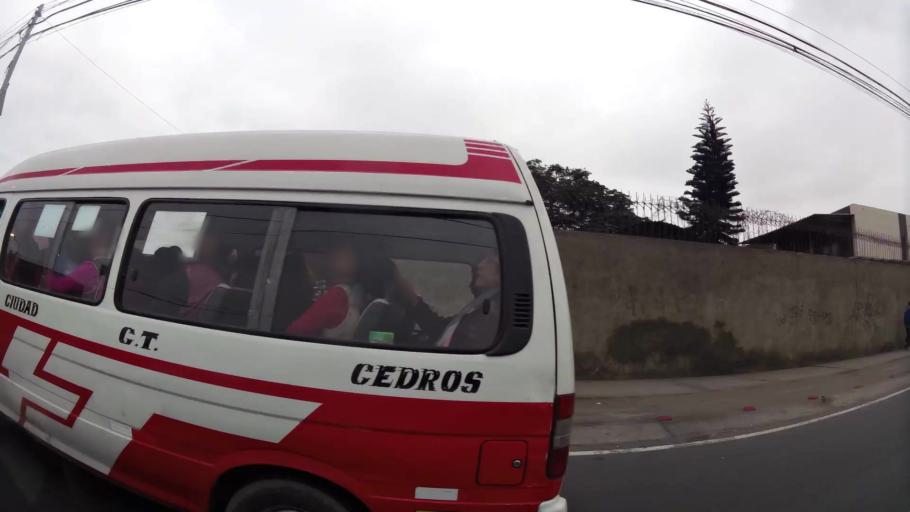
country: PE
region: Lima
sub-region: Lima
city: Surco
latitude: -12.1943
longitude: -77.0094
